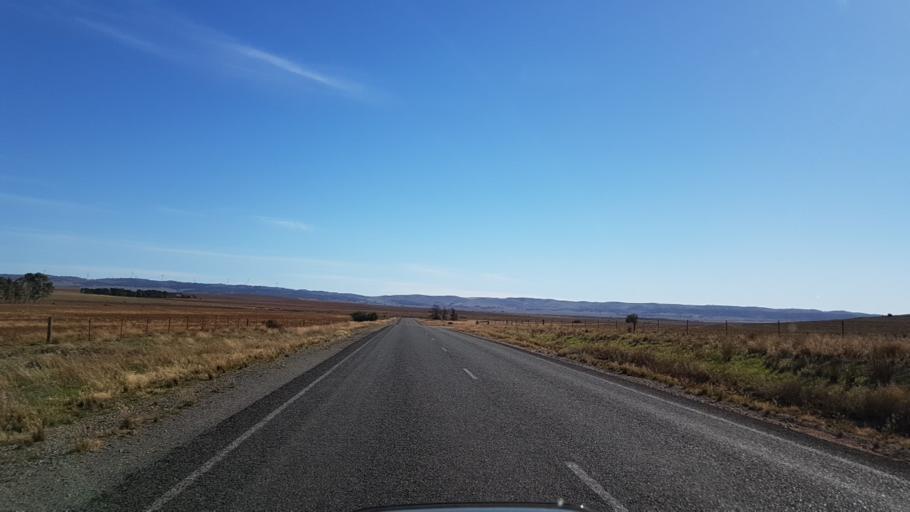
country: AU
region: South Australia
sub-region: Peterborough
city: Peterborough
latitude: -33.0174
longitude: 138.7040
